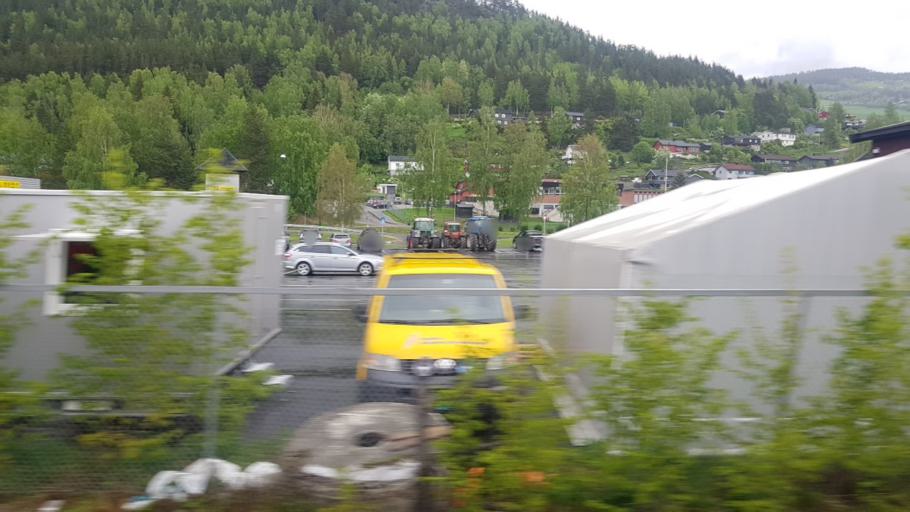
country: NO
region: Oppland
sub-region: Nord-Fron
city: Vinstra
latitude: 61.5840
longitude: 9.7605
